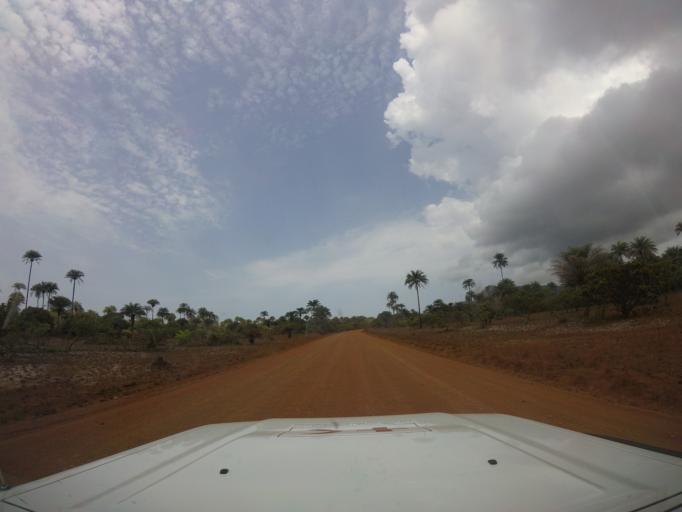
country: LR
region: Grand Cape Mount
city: Robertsport
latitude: 6.7031
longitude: -11.3189
